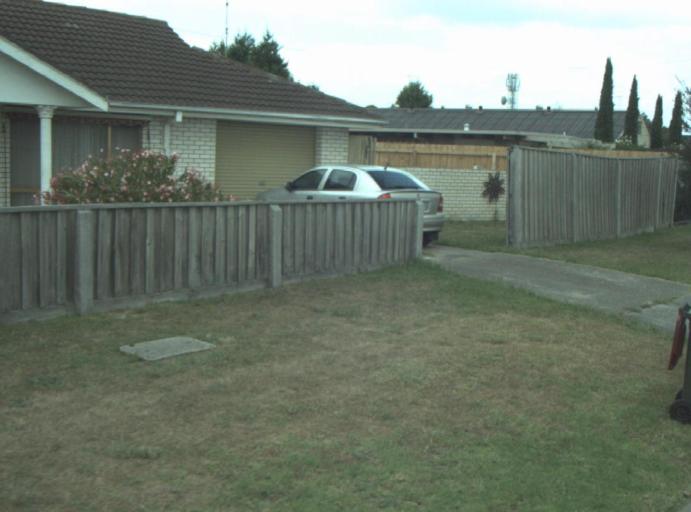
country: AU
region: Victoria
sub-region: Greater Geelong
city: East Geelong
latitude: -38.1696
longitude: 144.3993
